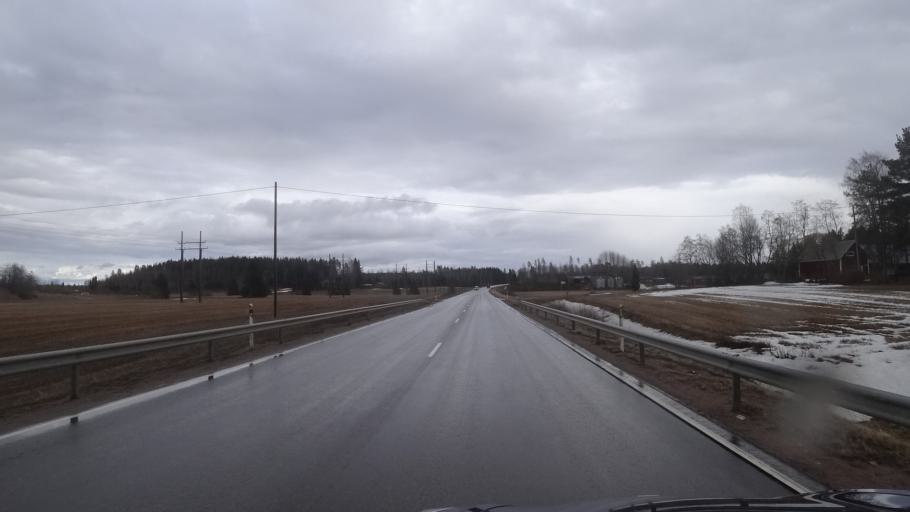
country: FI
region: Kymenlaakso
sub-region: Kouvola
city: Elimaeki
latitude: 60.7126
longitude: 26.4599
